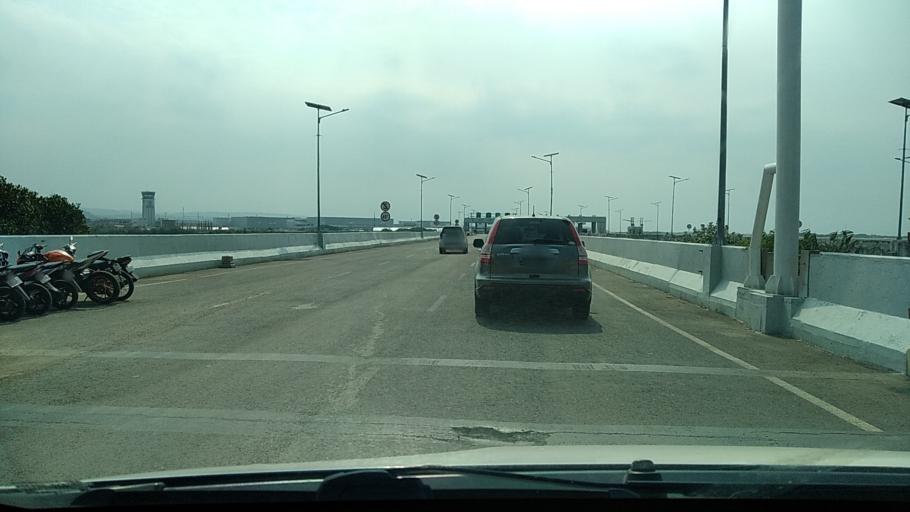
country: ID
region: Central Java
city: Semarang
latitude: -6.9634
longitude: 110.3835
